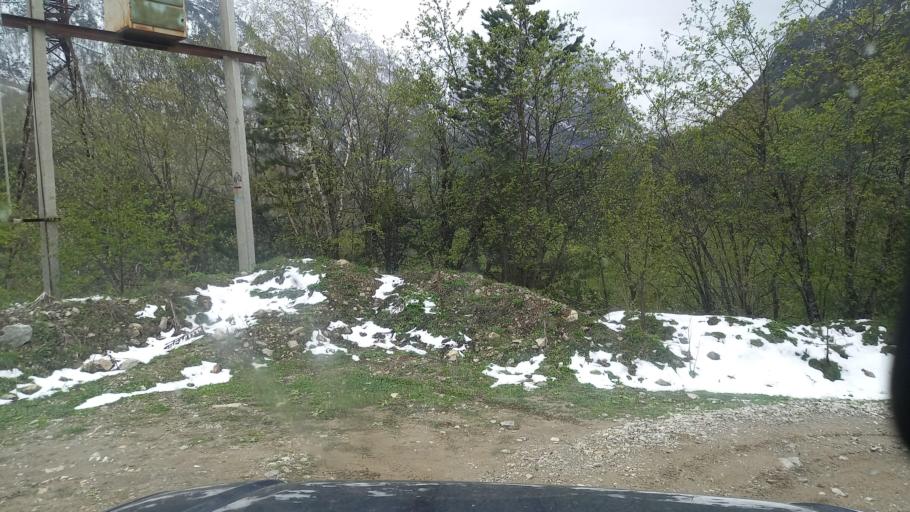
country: RU
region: North Ossetia
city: Mizur
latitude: 42.7995
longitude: 43.9320
